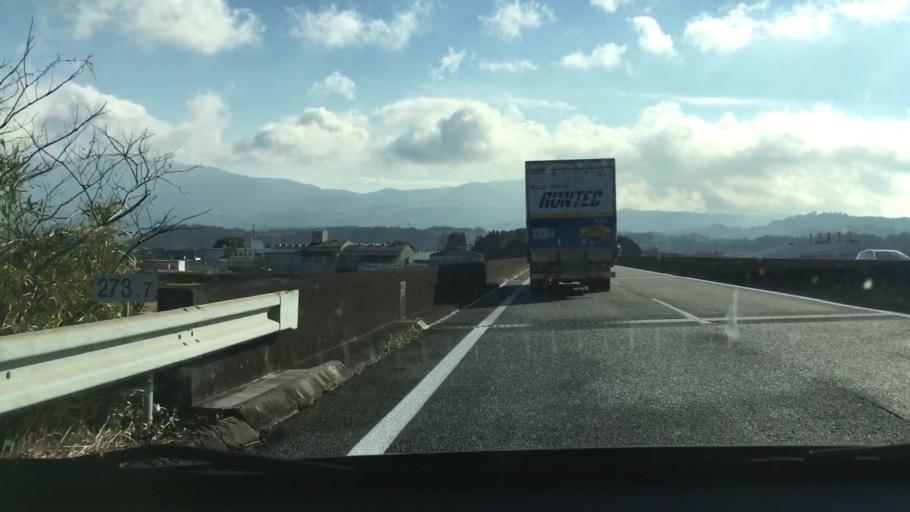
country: JP
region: Kumamoto
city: Hitoyoshi
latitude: 32.0555
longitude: 130.8024
